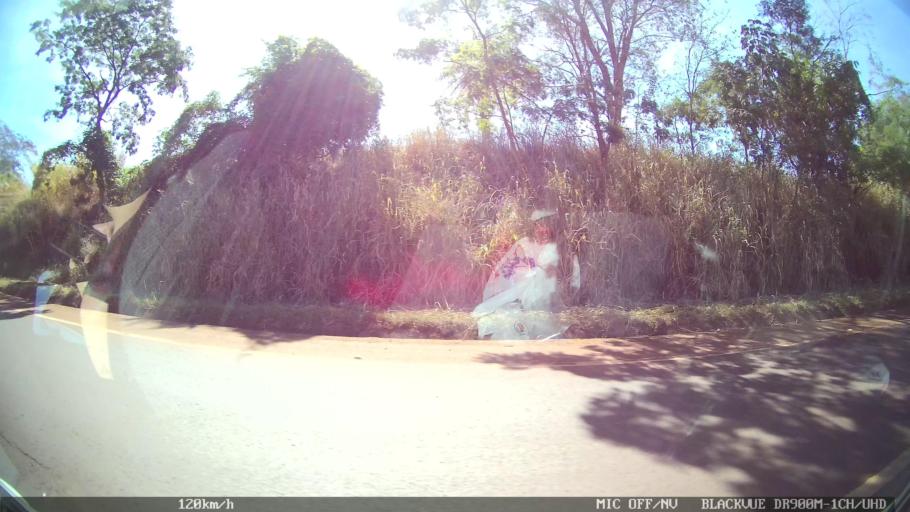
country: BR
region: Sao Paulo
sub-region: Sao Joaquim Da Barra
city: Sao Joaquim da Barra
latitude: -20.5396
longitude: -47.8154
